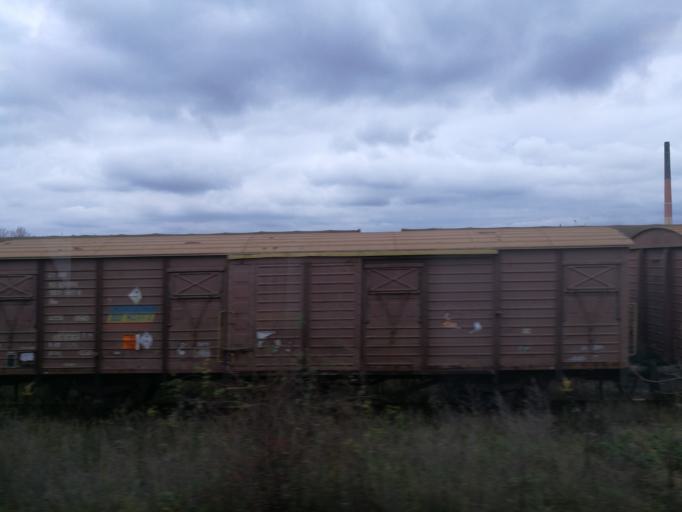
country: RO
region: Suceava
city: Suceava
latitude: 47.6634
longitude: 26.2837
